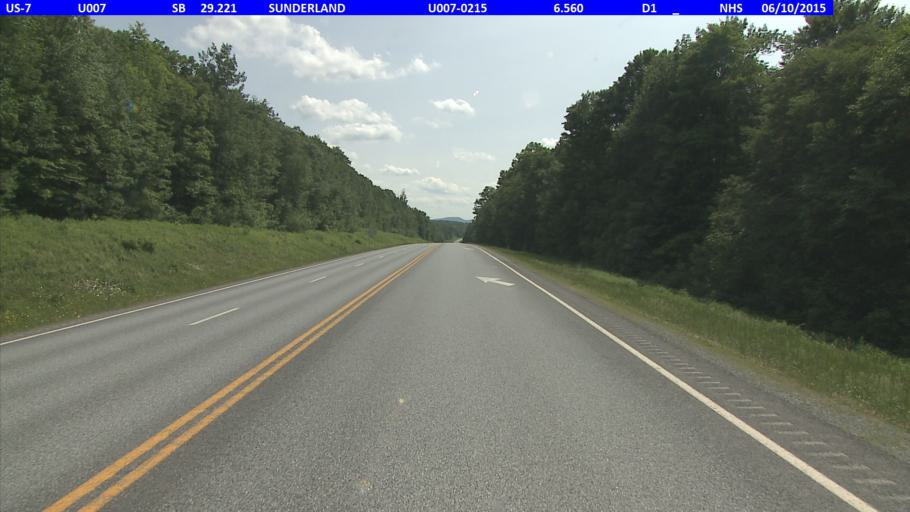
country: US
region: Vermont
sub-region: Bennington County
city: Manchester Center
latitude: 43.1117
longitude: -73.0883
